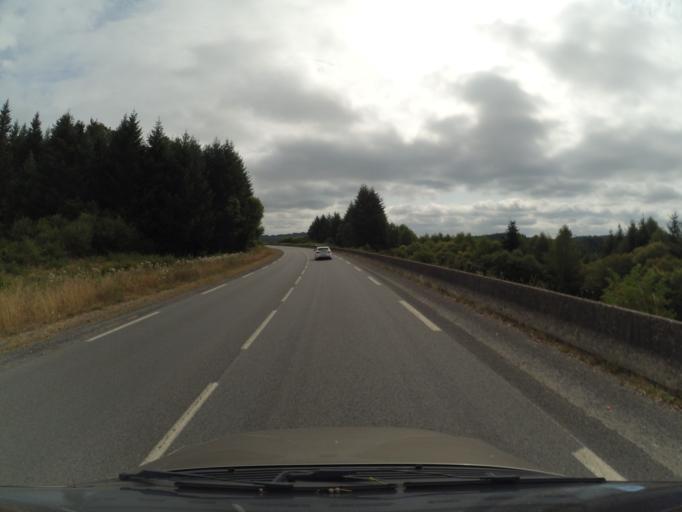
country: FR
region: Limousin
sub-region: Departement de la Correze
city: Ussel
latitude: 45.5211
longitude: 2.2873
